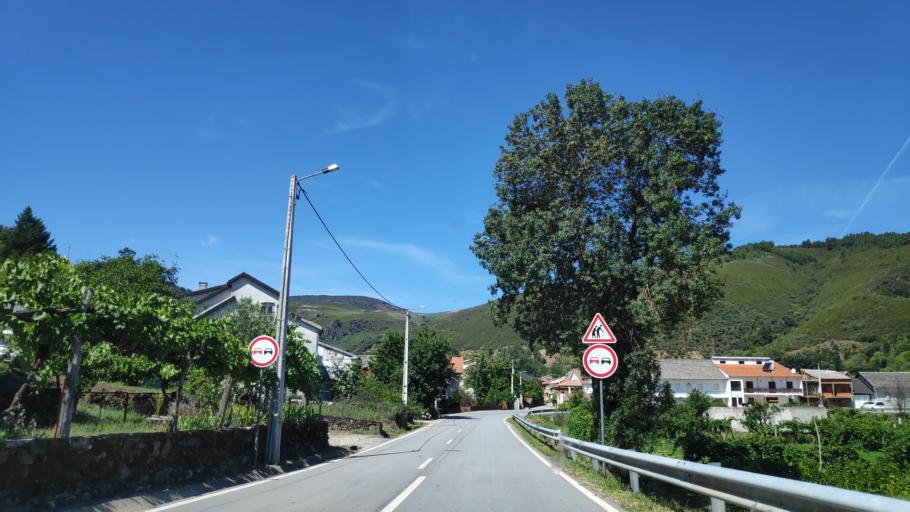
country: PT
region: Braganca
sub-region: Braganca Municipality
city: Braganca
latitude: 41.9006
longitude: -6.7341
